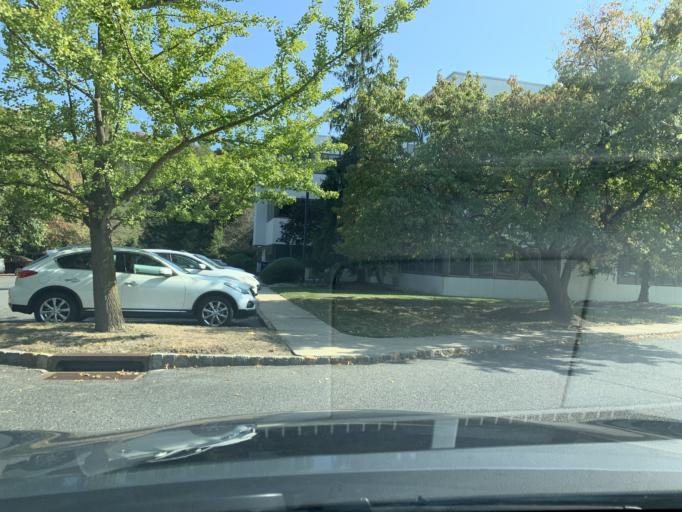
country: US
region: New Jersey
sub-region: Monmouth County
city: Shrewsbury
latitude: 40.3137
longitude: -74.0633
